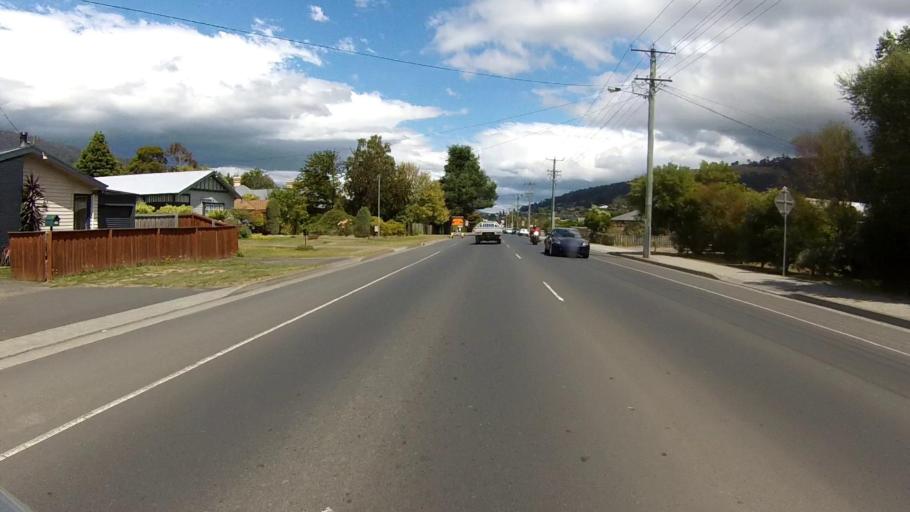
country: AU
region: Tasmania
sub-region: Huon Valley
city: Huonville
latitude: -43.0244
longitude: 147.0519
